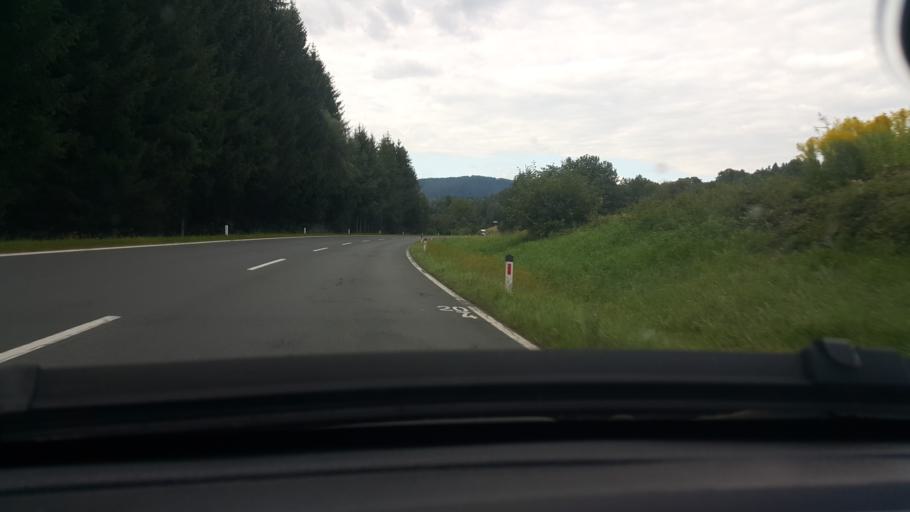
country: AT
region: Carinthia
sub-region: Politischer Bezirk Feldkirchen
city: Feldkirchen in Karnten
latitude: 46.7019
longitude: 14.1192
